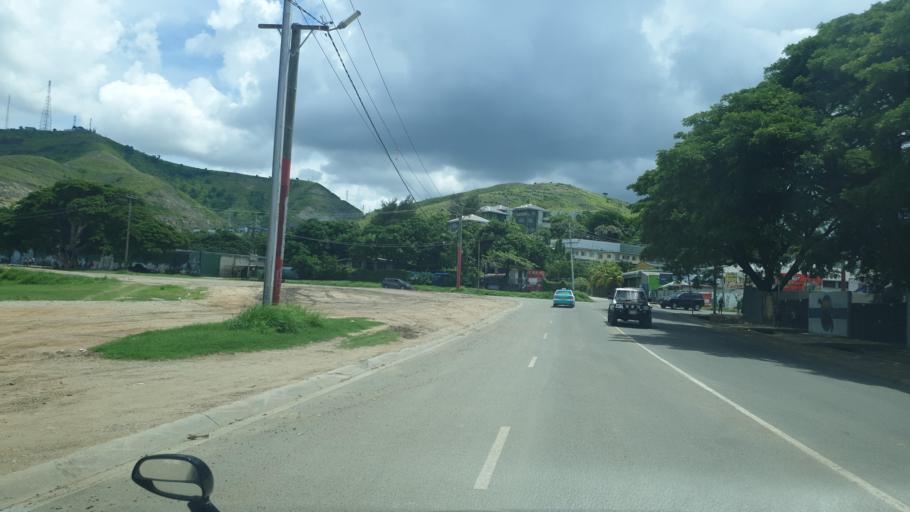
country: PG
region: National Capital
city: Port Moresby
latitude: -9.4657
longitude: 147.1573
